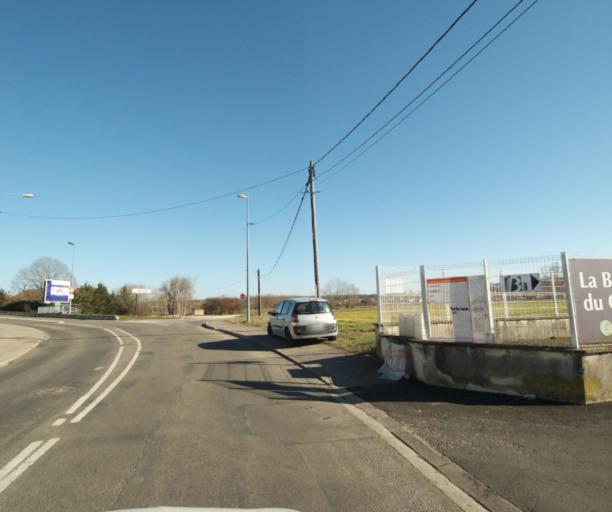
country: FR
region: Lorraine
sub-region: Departement de Meurthe-et-Moselle
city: Saulxures-les-Nancy
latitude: 48.6834
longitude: 6.2327
